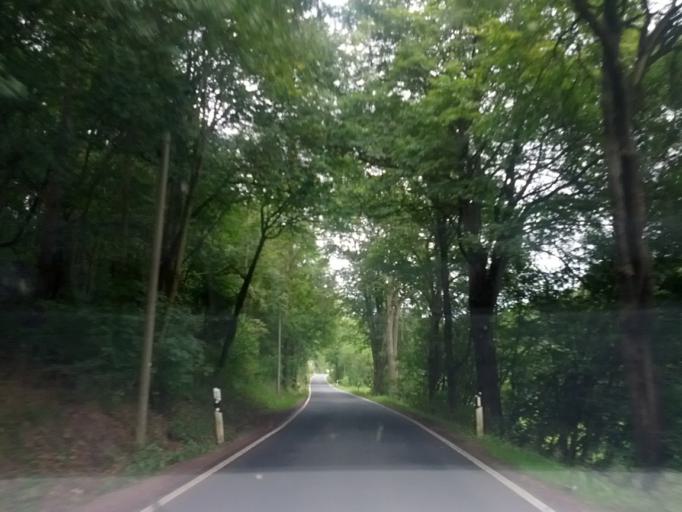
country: DE
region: Thuringia
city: Wolfsburg-Unkeroda
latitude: 50.8841
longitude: 10.2586
